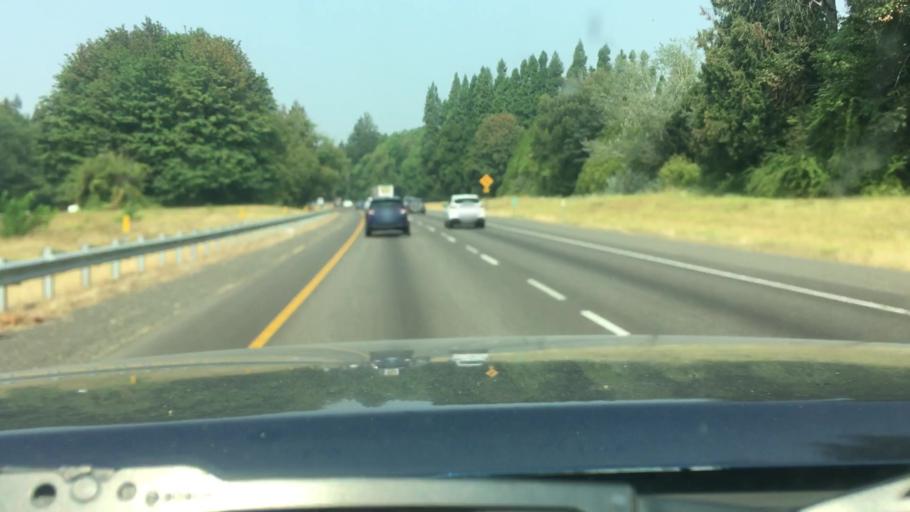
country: US
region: Oregon
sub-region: Clackamas County
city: Stafford
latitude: 45.3620
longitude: -122.6701
